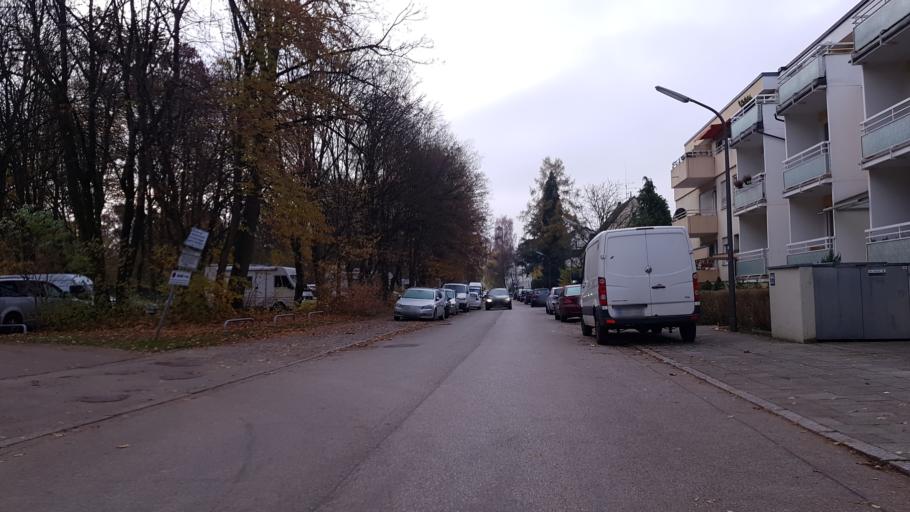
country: DE
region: Bavaria
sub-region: Upper Bavaria
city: Unterhaching
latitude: 48.1074
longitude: 11.6079
